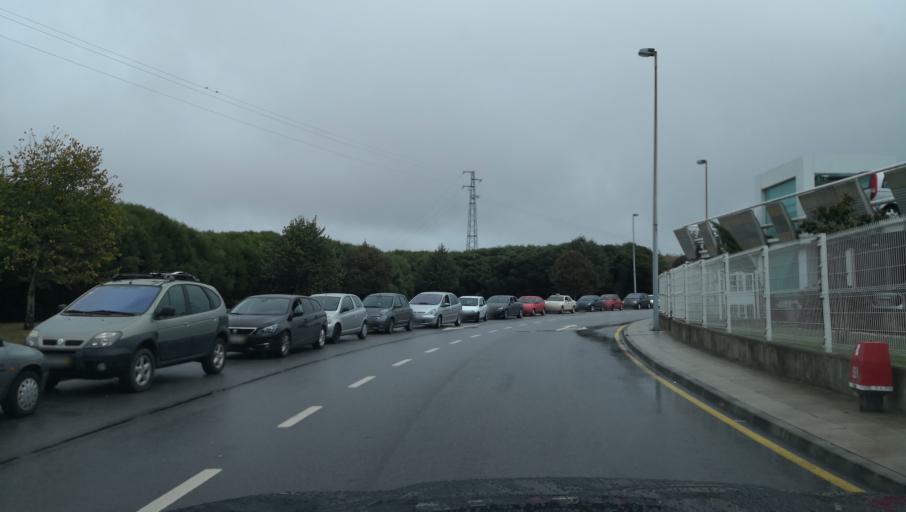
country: PT
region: Porto
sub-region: Matosinhos
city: Santa Cruz do Bispo
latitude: 41.2423
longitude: -8.6711
